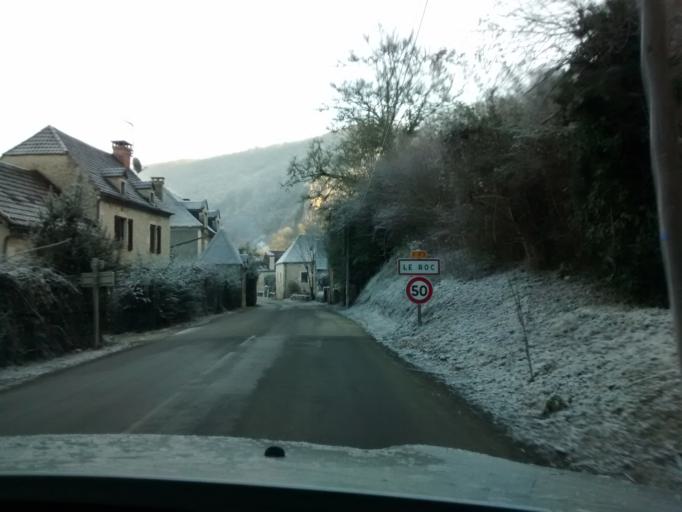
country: FR
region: Midi-Pyrenees
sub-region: Departement du Lot
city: Souillac
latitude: 44.8647
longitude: 1.4378
